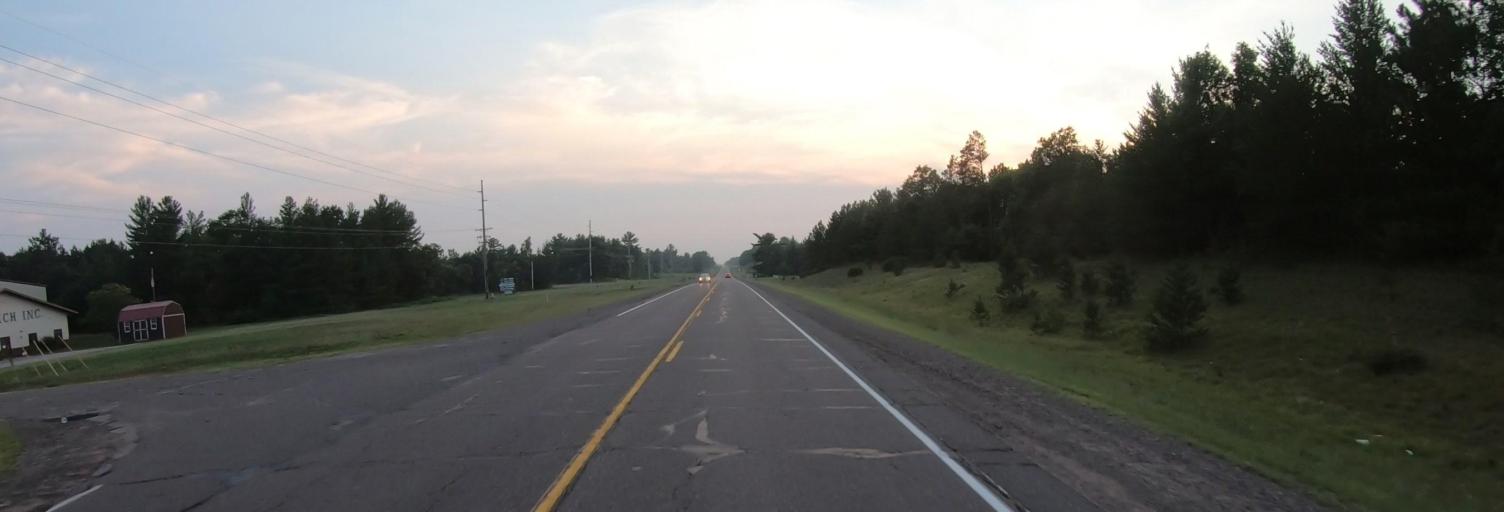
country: US
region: Wisconsin
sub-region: Burnett County
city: Grantsburg
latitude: 45.7732
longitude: -92.7177
